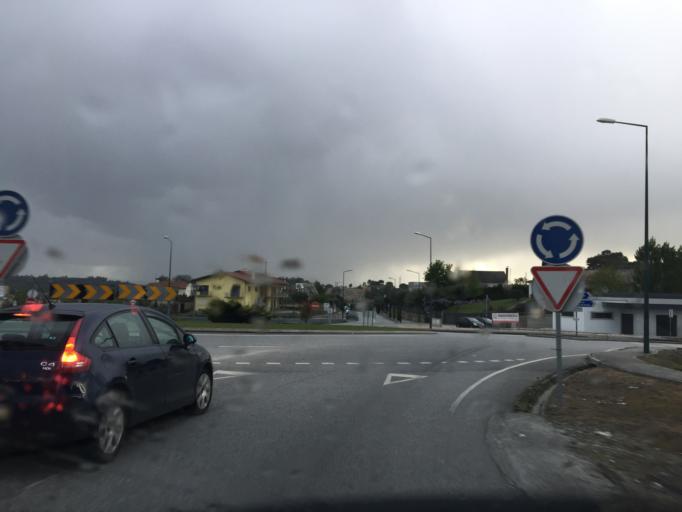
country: PT
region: Viseu
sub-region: Viseu
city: Viseu
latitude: 40.6167
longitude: -7.9556
